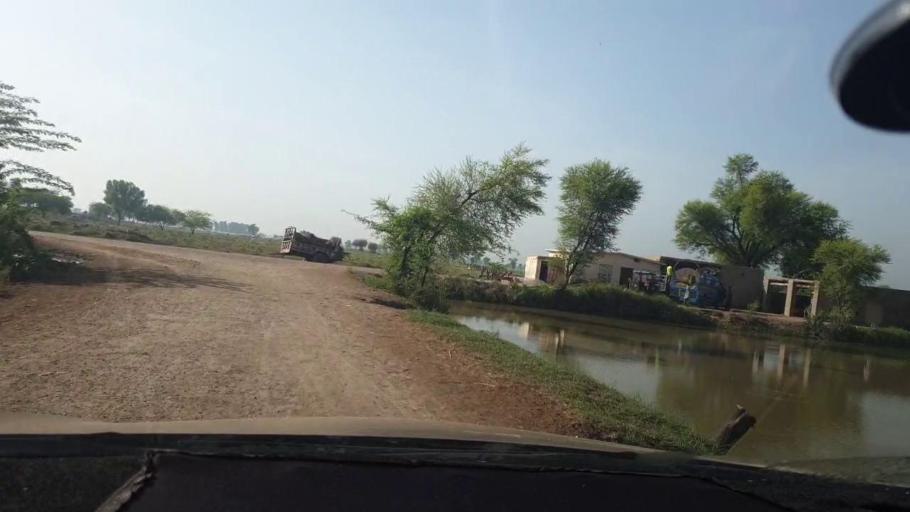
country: PK
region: Sindh
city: Kambar
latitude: 27.6447
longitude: 68.0420
